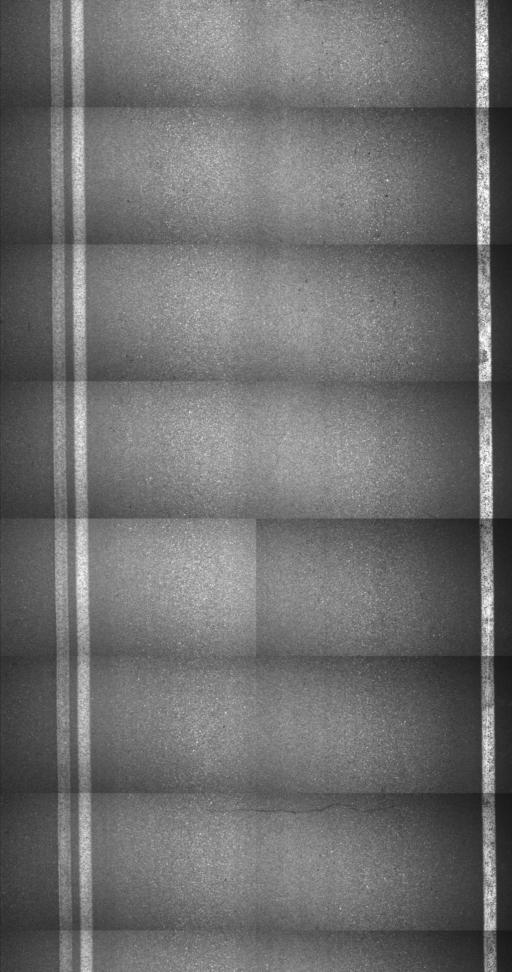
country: US
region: New Hampshire
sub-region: Grafton County
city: Woodsville
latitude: 44.1883
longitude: -72.0668
